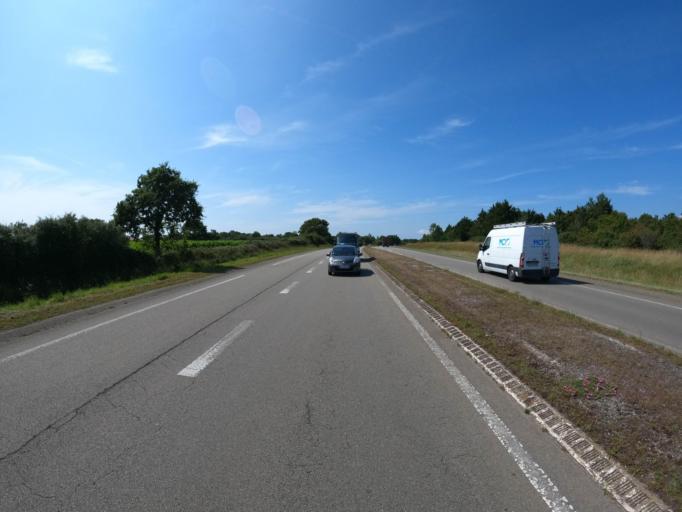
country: FR
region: Pays de la Loire
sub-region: Departement de la Loire-Atlantique
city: La Bernerie-en-Retz
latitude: 47.0896
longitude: -2.0315
